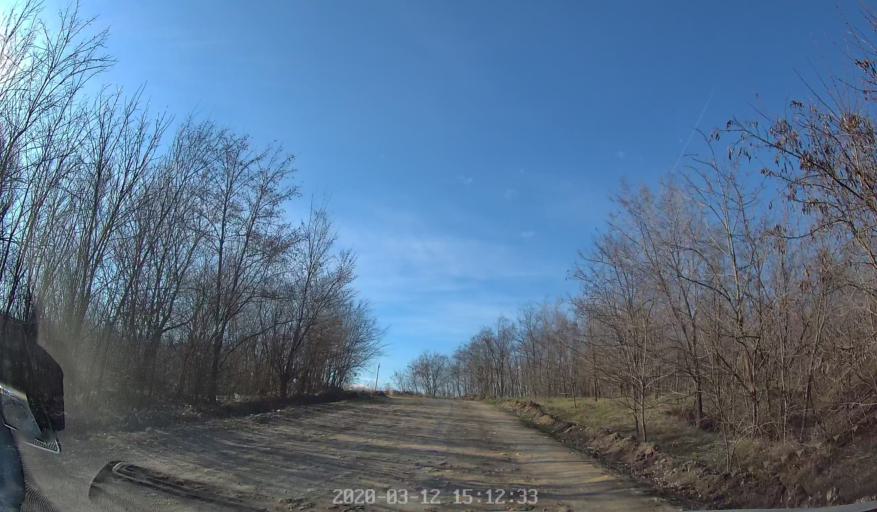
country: MD
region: Chisinau
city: Ciorescu
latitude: 47.2292
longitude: 28.9709
